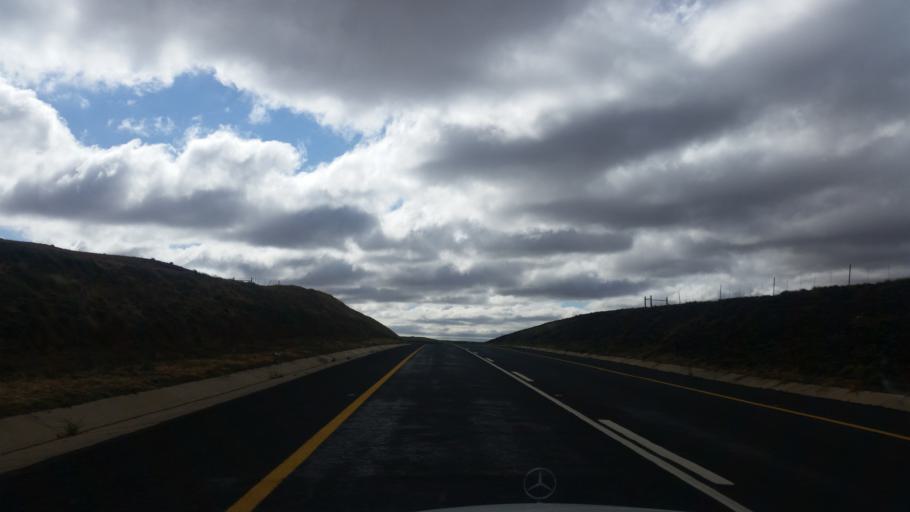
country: ZA
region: Orange Free State
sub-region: Thabo Mofutsanyana District Municipality
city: Phuthaditjhaba
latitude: -28.3121
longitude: 28.7630
